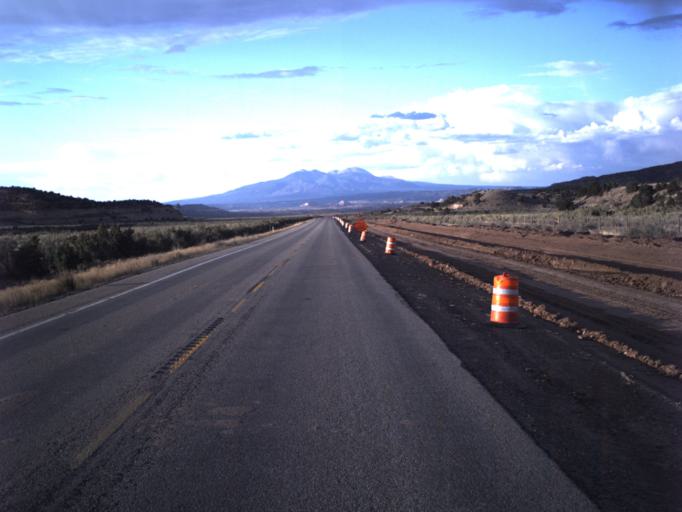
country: US
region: Utah
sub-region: San Juan County
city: Monticello
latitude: 38.0266
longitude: -109.3470
